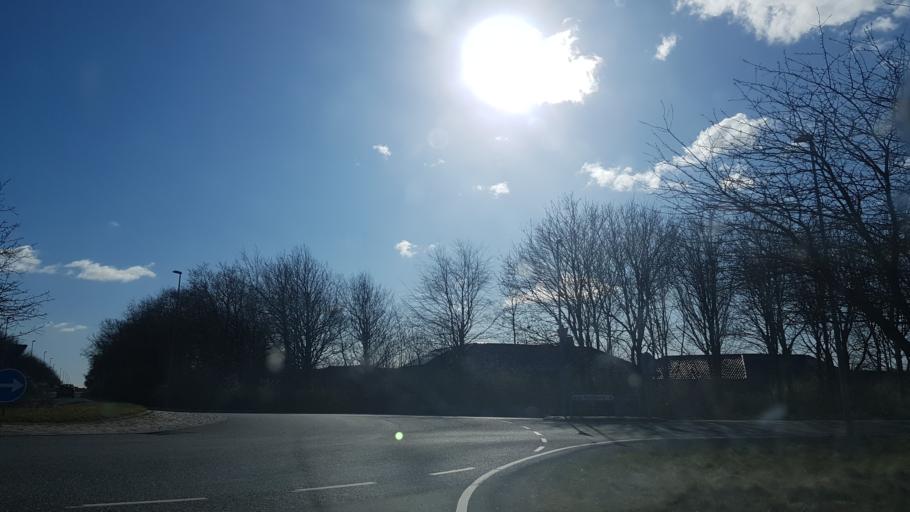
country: DK
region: South Denmark
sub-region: Fano Kommune
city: Nordby
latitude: 55.5347
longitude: 8.3625
